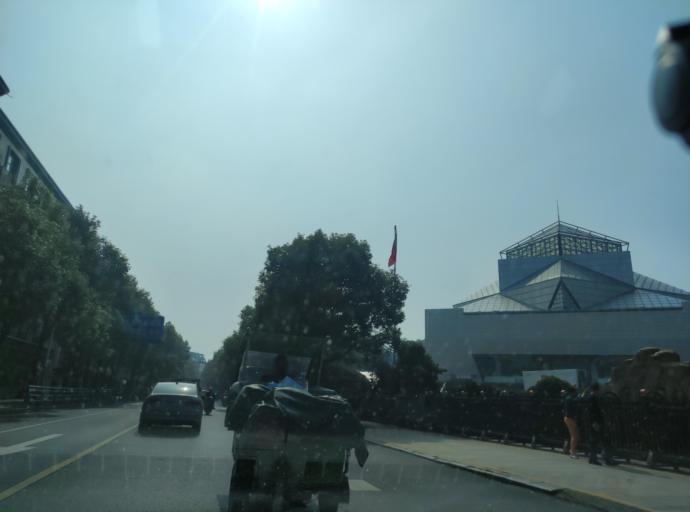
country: CN
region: Jiangxi Sheng
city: Pingxiang
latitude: 27.6440
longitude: 113.8547
